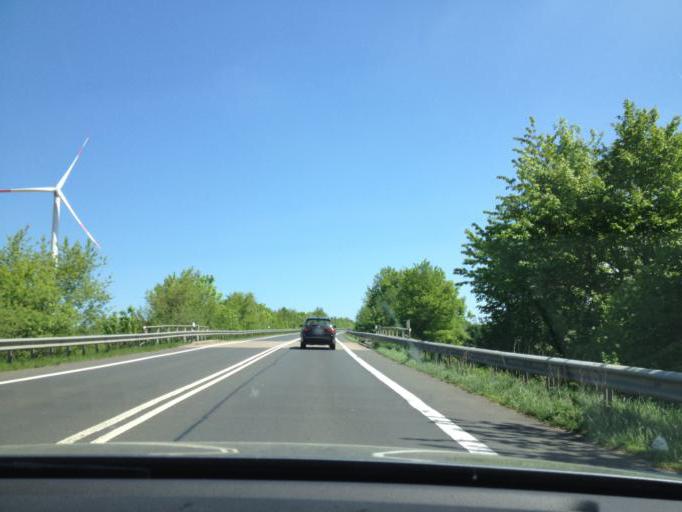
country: DE
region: Rheinland-Pfalz
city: Bitburg
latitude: 49.9915
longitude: 6.5234
